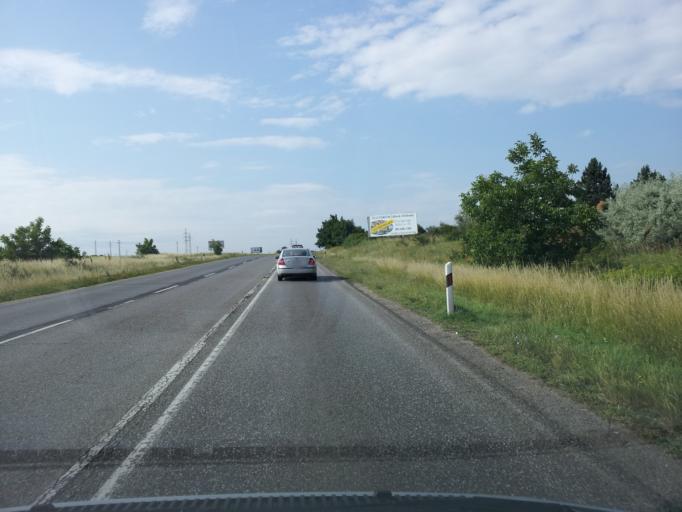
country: HU
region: Veszprem
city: Veszprem
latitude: 47.0962
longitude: 17.9332
